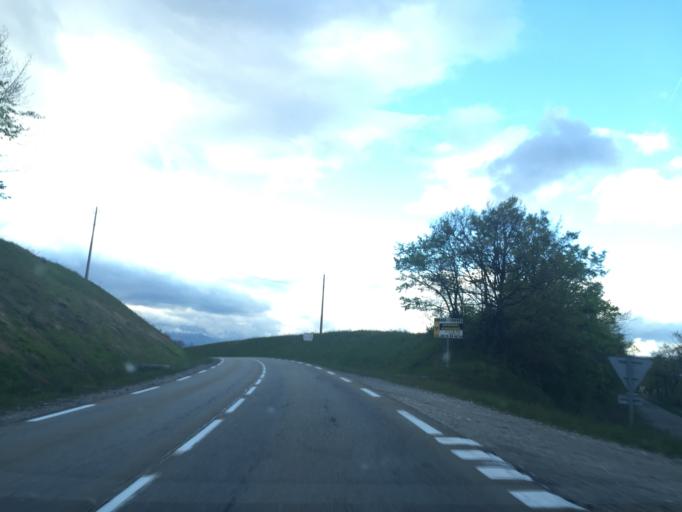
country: FR
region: Rhone-Alpes
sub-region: Departement de l'Isere
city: Mens
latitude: 44.7840
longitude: 5.6472
